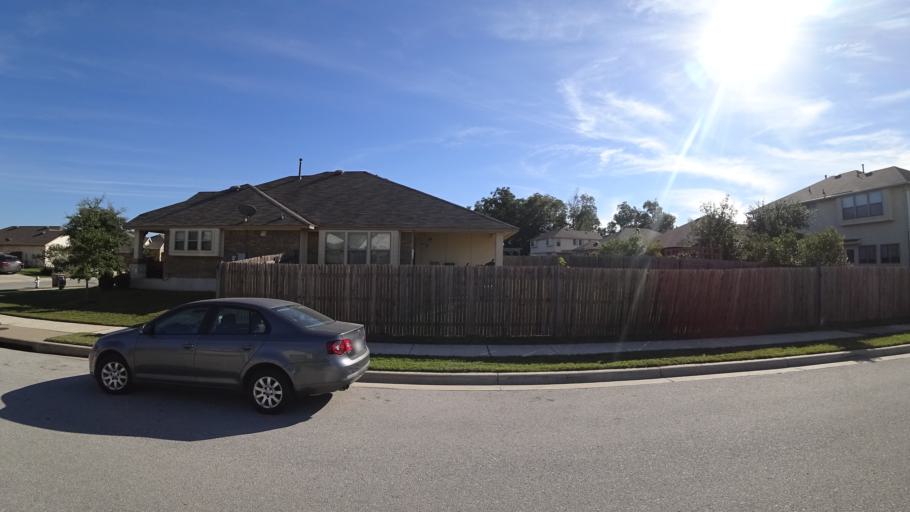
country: US
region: Texas
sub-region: Travis County
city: Austin
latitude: 30.2611
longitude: -97.6668
